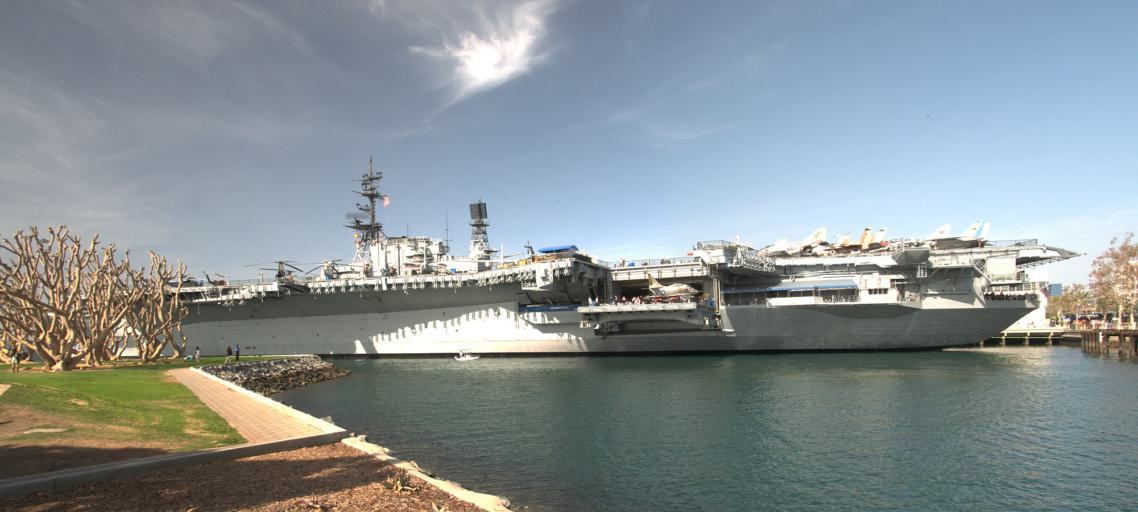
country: US
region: California
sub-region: San Diego County
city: San Diego
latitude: 32.7126
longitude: -117.1739
